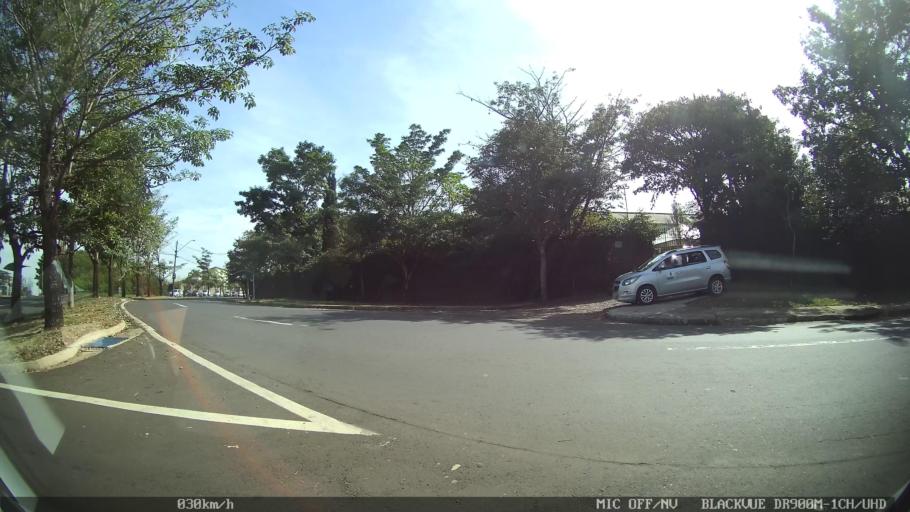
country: BR
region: Sao Paulo
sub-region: Piracicaba
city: Piracicaba
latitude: -22.7489
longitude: -47.6157
